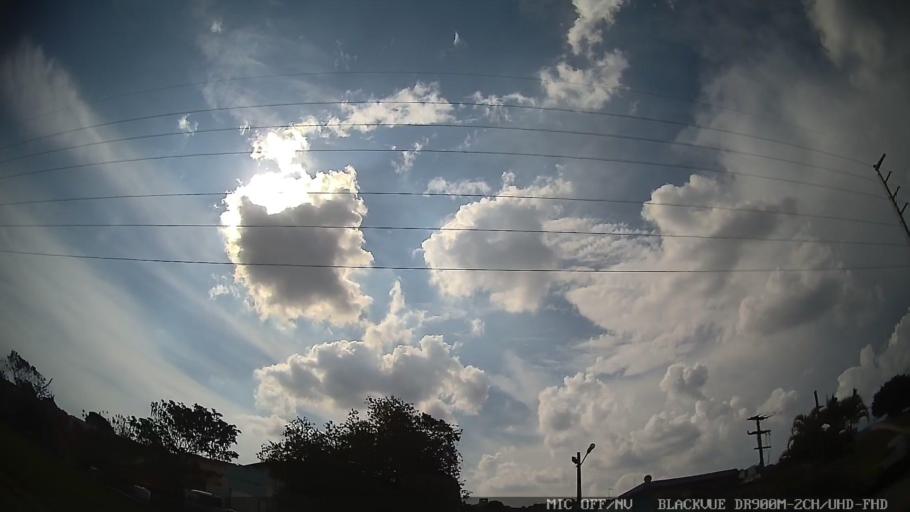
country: BR
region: Sao Paulo
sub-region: Braganca Paulista
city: Braganca Paulista
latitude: -22.9194
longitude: -46.5506
